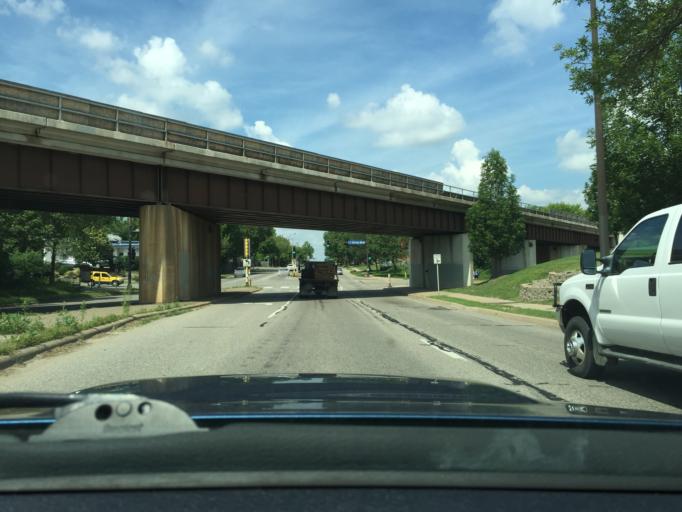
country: US
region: Minnesota
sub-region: Ramsey County
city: Lauderdale
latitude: 44.9914
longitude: -93.2260
